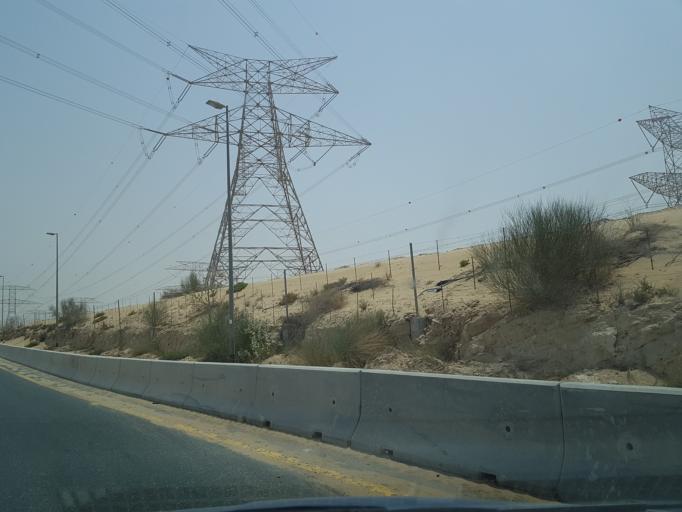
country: AE
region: Dubai
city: Dubai
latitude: 25.0358
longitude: 55.2960
